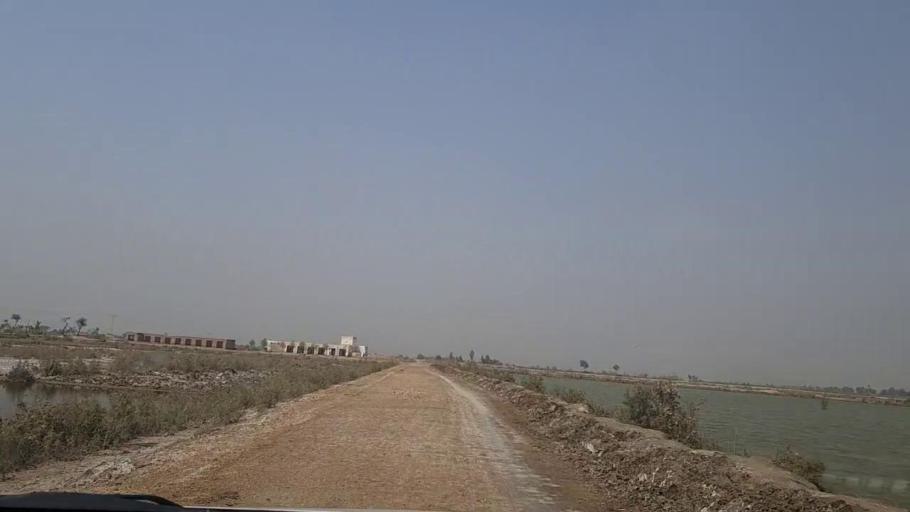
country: PK
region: Sindh
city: Pithoro
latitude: 25.5554
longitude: 69.2114
